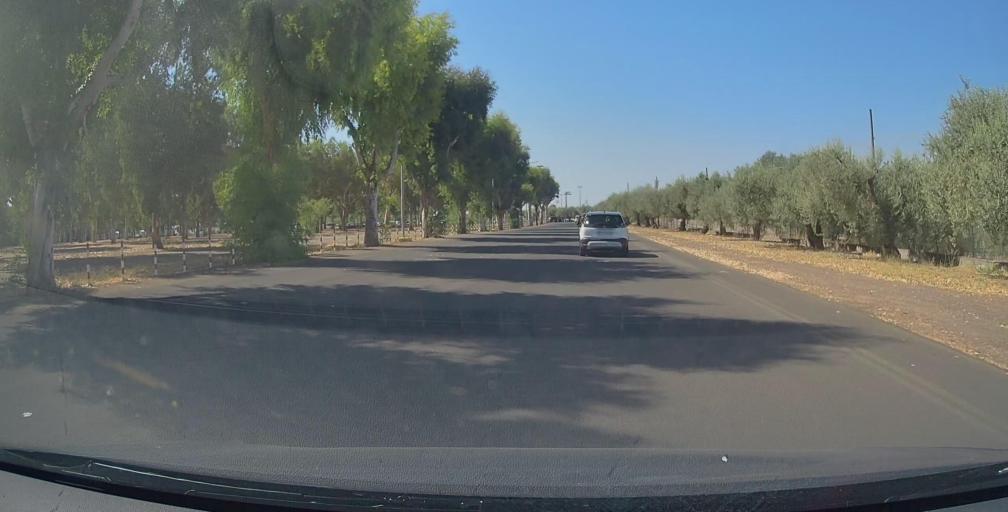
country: IT
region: Sicily
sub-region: Catania
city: Palazzolo
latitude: 37.5387
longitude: 14.9316
